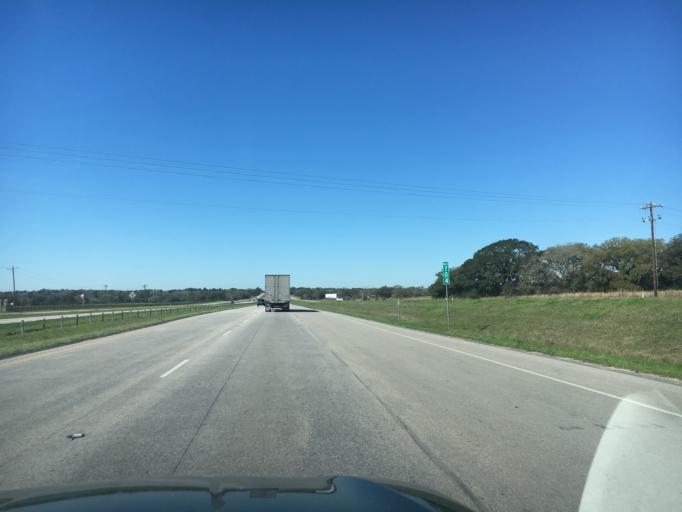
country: US
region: Texas
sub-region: Colorado County
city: Columbus
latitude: 29.7237
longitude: -96.4190
